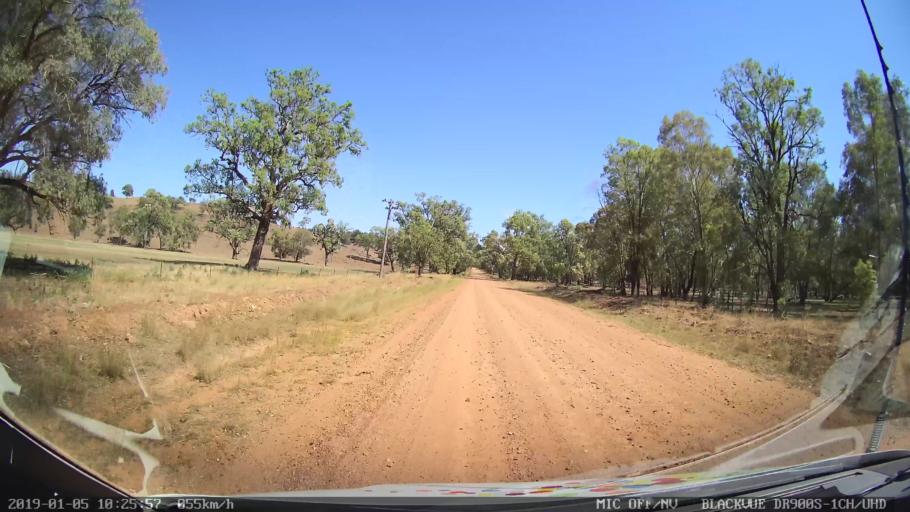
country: AU
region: New South Wales
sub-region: Gilgandra
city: Gilgandra
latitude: -31.5573
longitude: 148.9570
